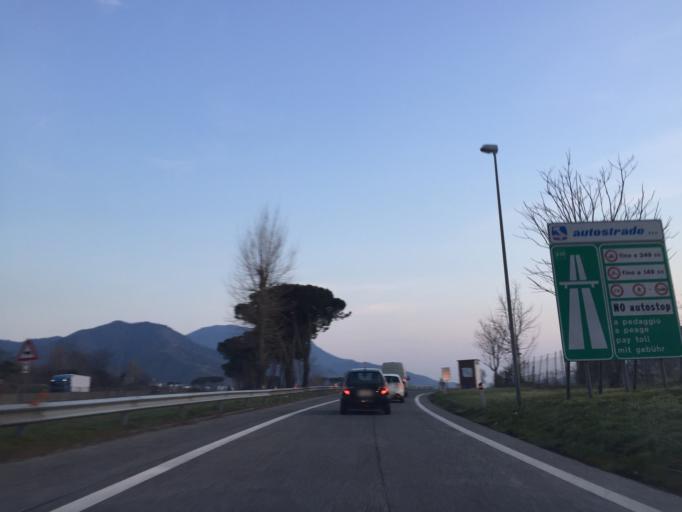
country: IT
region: Campania
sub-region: Provincia di Salerno
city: Fisciano
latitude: 40.7759
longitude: 14.7841
